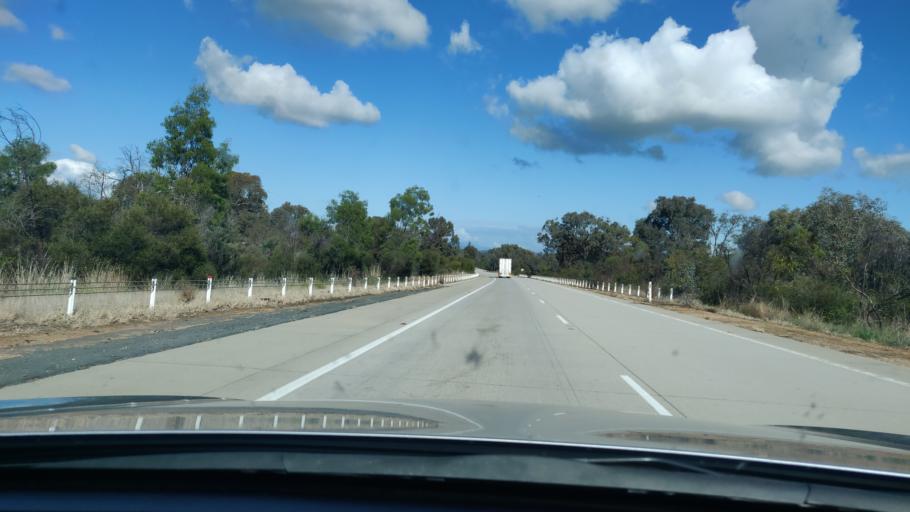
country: AU
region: New South Wales
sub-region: Greater Hume Shire
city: Holbrook
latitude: -35.8507
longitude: 147.1924
